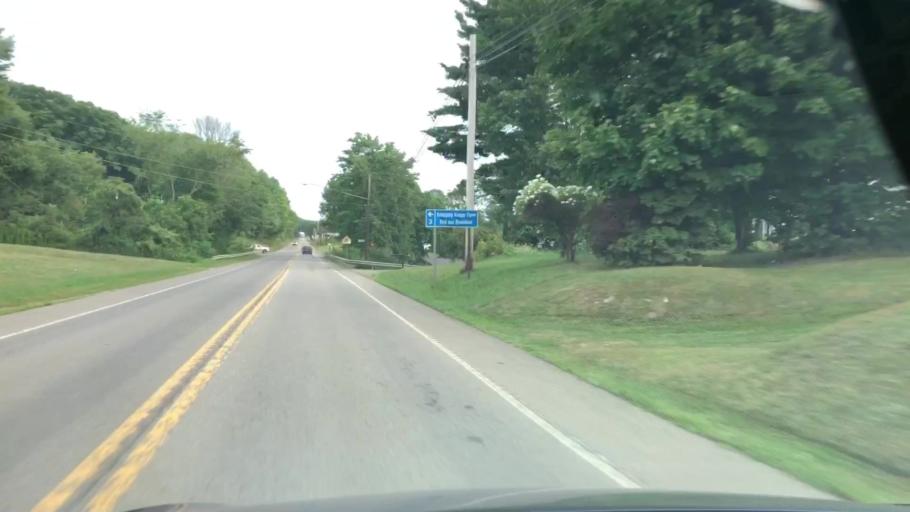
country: US
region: Pennsylvania
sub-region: Crawford County
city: Titusville
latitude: 41.6545
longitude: -79.7249
